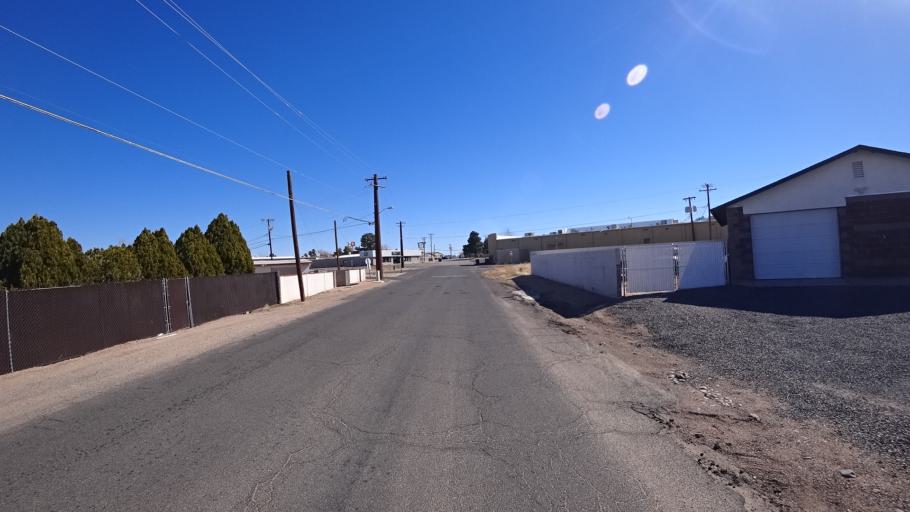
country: US
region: Arizona
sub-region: Mohave County
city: Kingman
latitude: 35.2104
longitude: -114.0195
